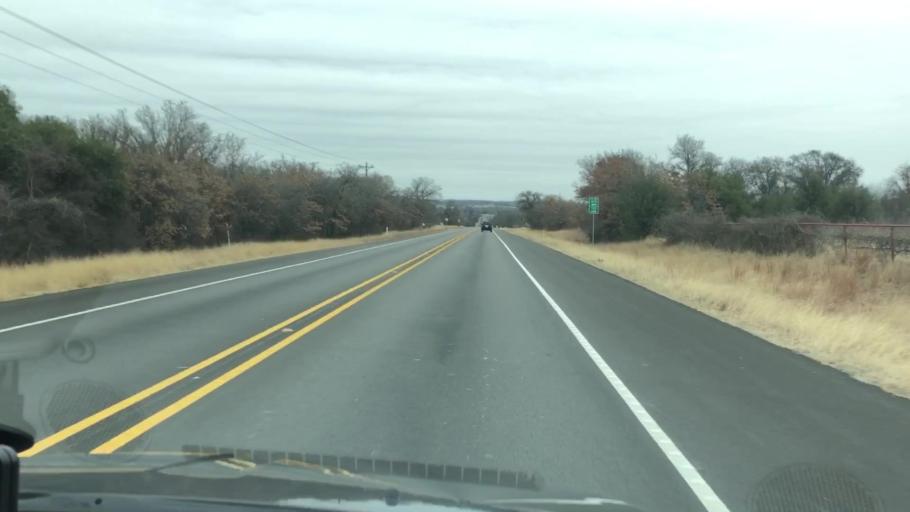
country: US
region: Texas
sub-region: Erath County
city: Stephenville
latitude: 32.4009
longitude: -98.1609
